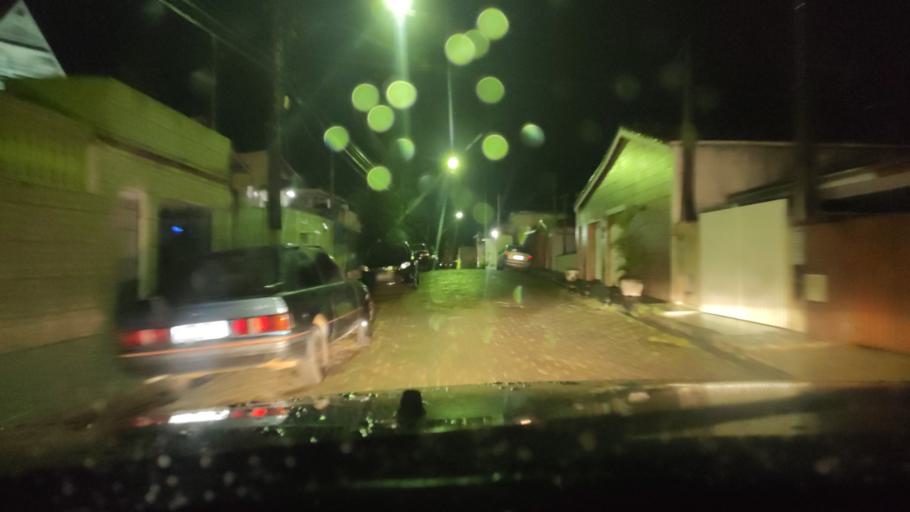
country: BR
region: Sao Paulo
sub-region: Sao Sebastiao
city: Sao Sebastiao
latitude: -23.7542
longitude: -45.4144
